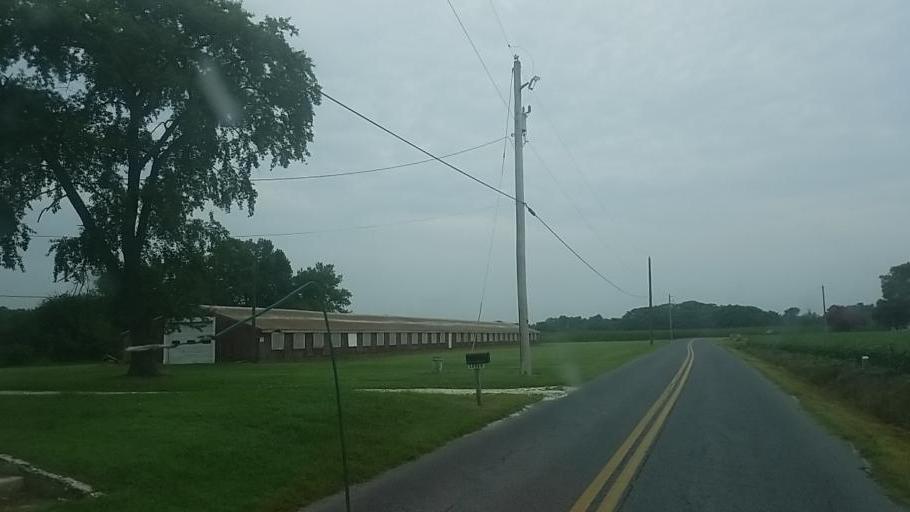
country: US
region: Delaware
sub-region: Sussex County
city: Selbyville
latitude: 38.4359
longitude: -75.1947
